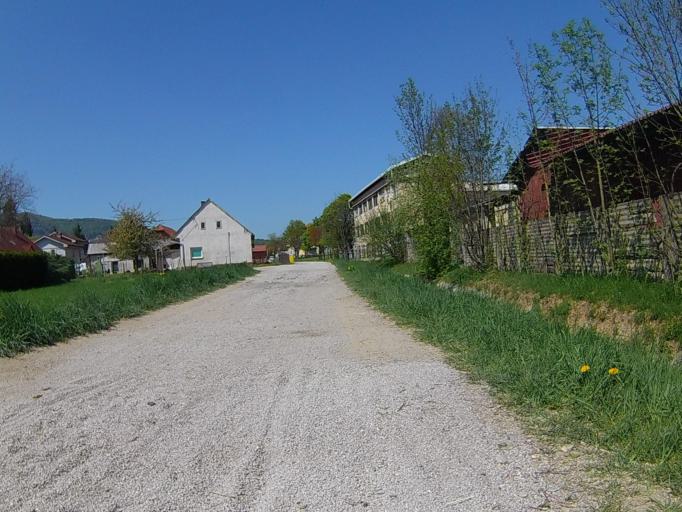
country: SI
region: Hoce-Slivnica
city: Spodnje Hoce
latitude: 46.4972
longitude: 15.6469
